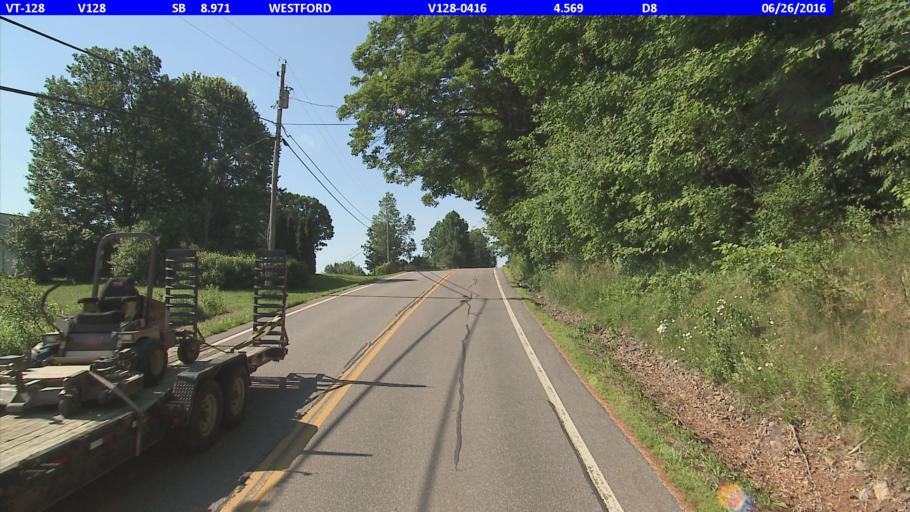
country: US
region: Vermont
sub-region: Chittenden County
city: Milton
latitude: 44.6202
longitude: -73.0156
